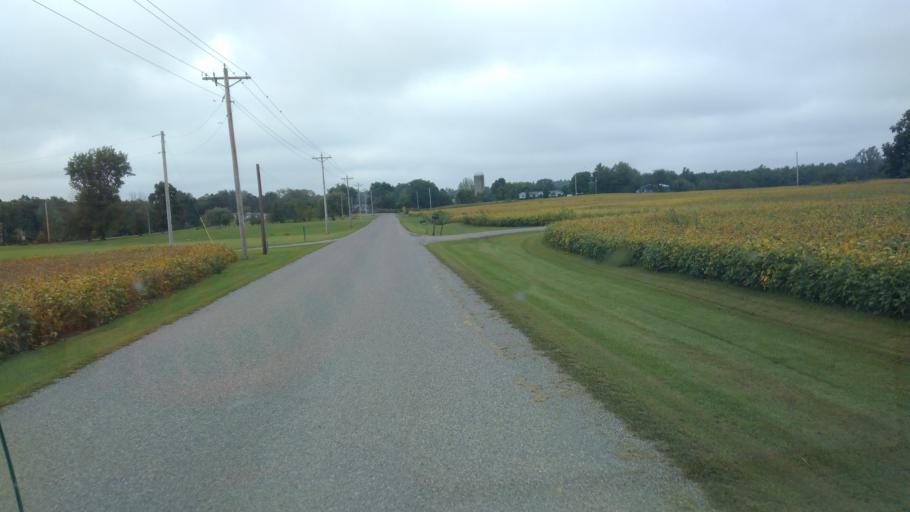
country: US
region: Ohio
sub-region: Hardin County
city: Kenton
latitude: 40.5762
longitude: -83.6611
